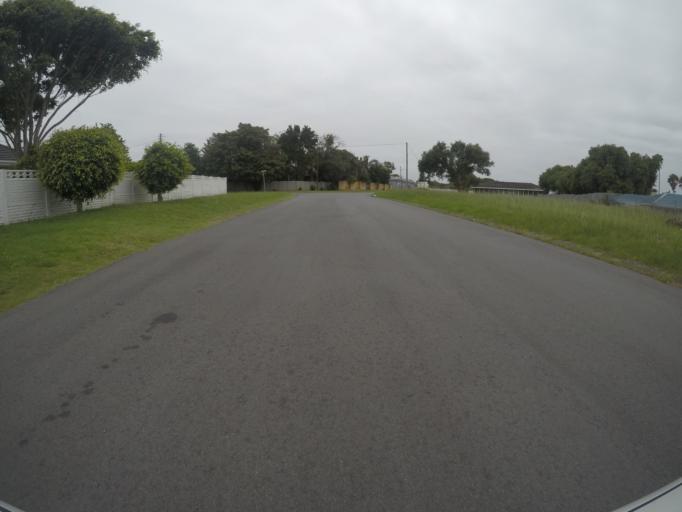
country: ZA
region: Eastern Cape
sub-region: Buffalo City Metropolitan Municipality
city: East London
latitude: -32.9687
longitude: 27.9380
